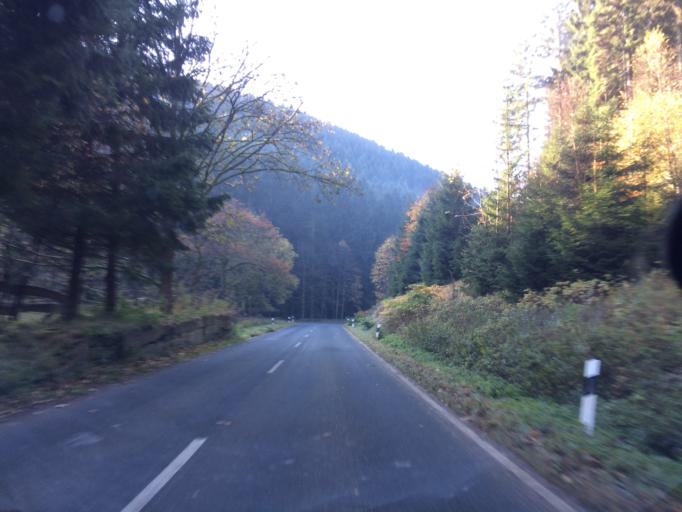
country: DE
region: Lower Saxony
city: Sankt Andreasberg
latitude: 51.6971
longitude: 10.5103
